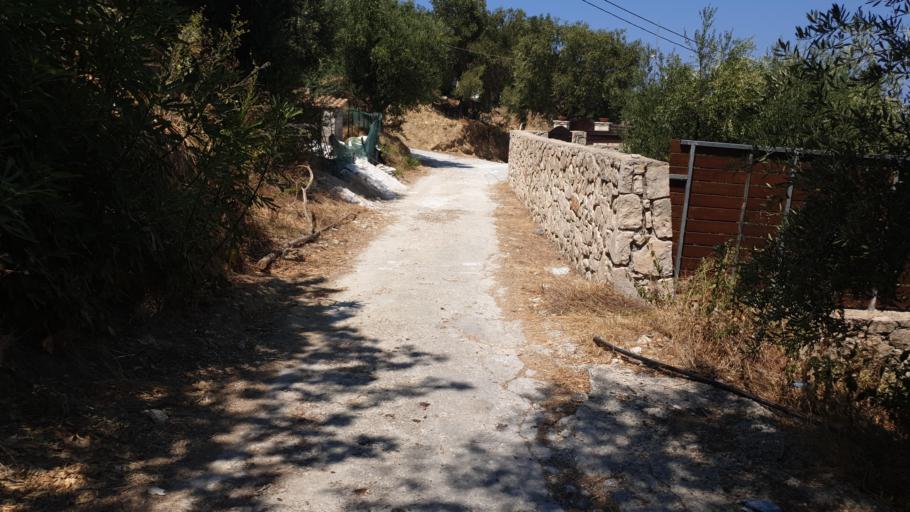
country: GR
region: Ionian Islands
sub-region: Nomos Zakynthou
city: Zakynthos
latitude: 37.7463
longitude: 20.9460
